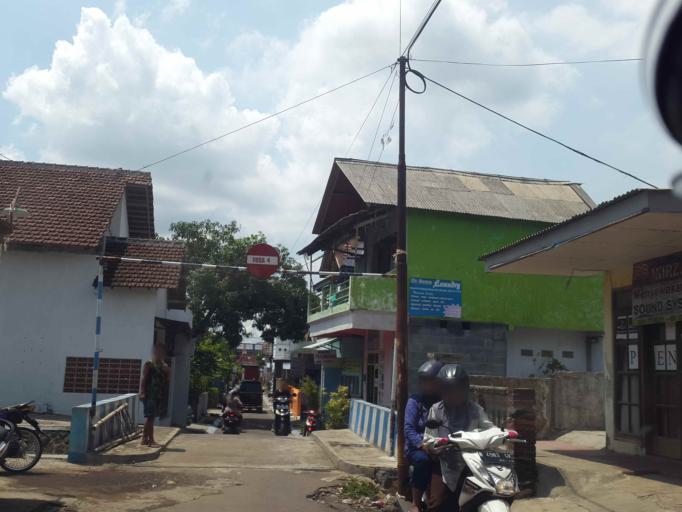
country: ID
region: East Java
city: Singosari
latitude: -7.8931
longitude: 112.6640
